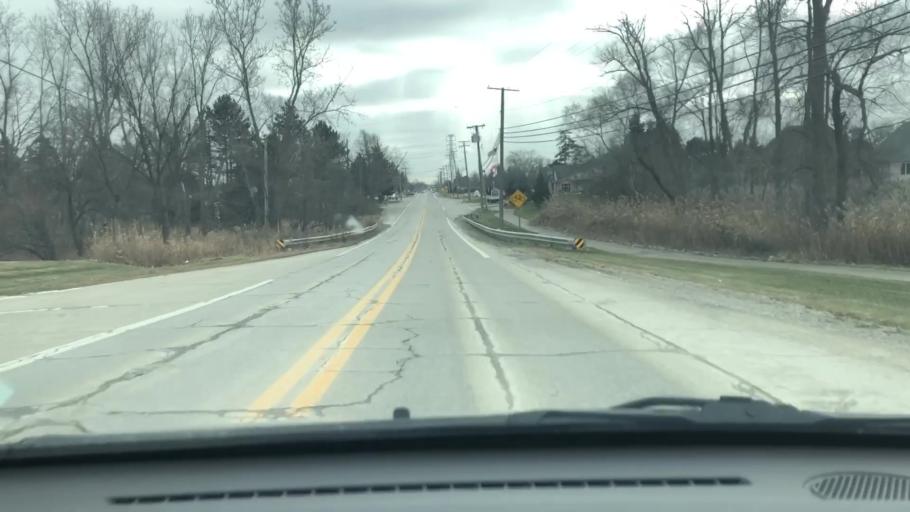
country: US
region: Michigan
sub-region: Macomb County
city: Shelby
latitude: 42.7375
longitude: -83.0365
